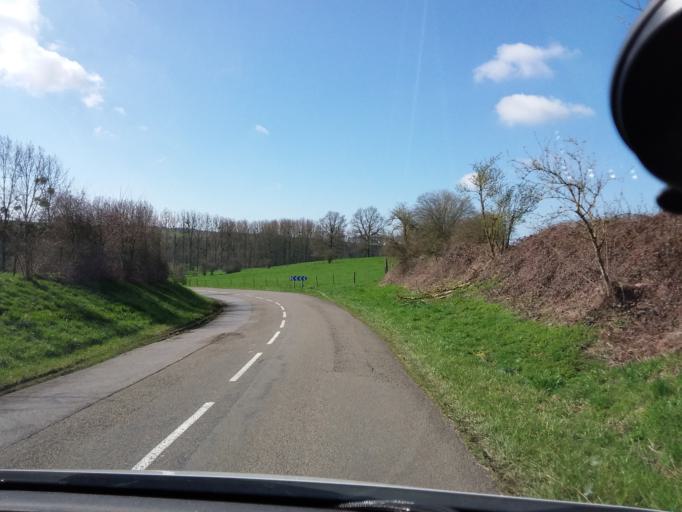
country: FR
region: Picardie
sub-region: Departement de l'Aisne
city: Origny-en-Thierache
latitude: 49.7993
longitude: 4.0081
